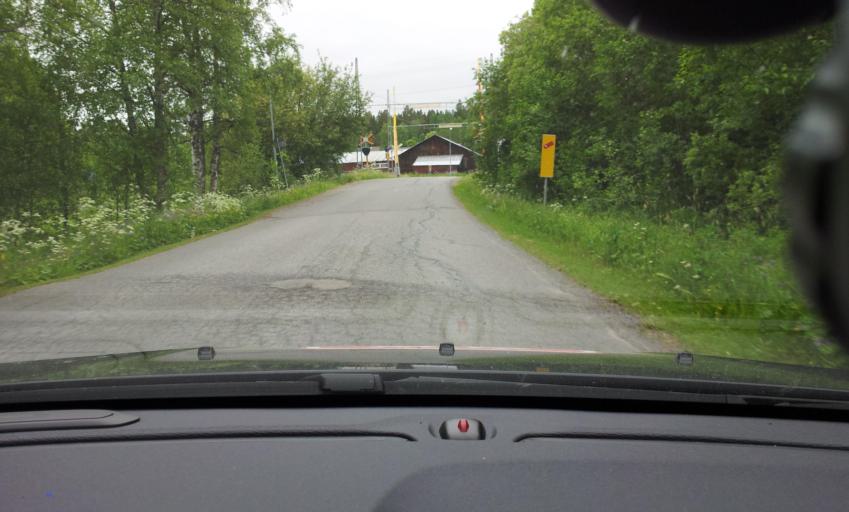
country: SE
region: Jaemtland
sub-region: Are Kommun
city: Jarpen
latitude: 63.3052
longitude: 13.6786
